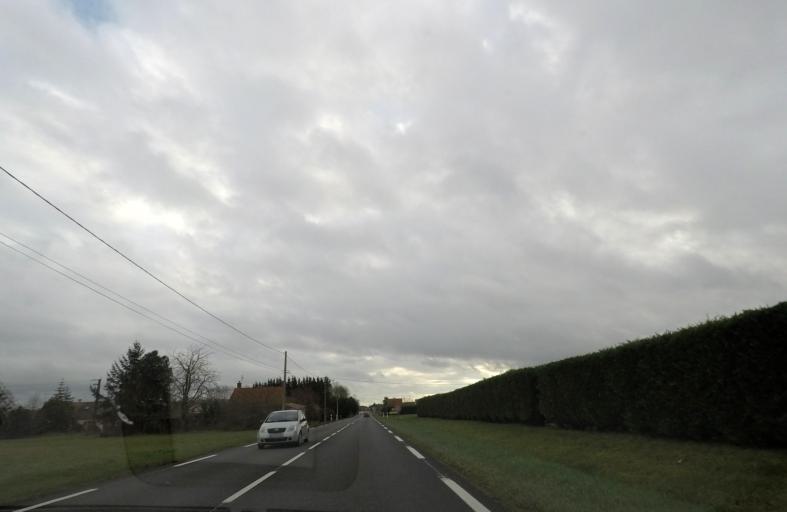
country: FR
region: Centre
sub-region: Departement du Loir-et-Cher
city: Soings-en-Sologne
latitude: 47.4650
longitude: 1.5149
